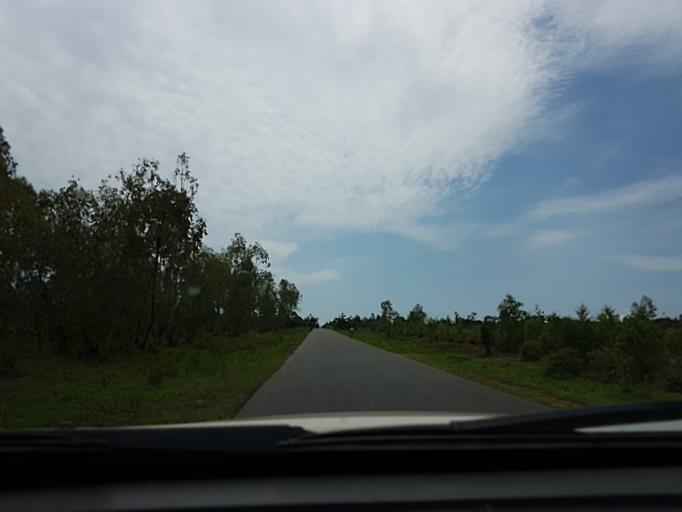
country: CD
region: South Kivu
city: Uvira
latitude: -3.1912
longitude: 29.1537
